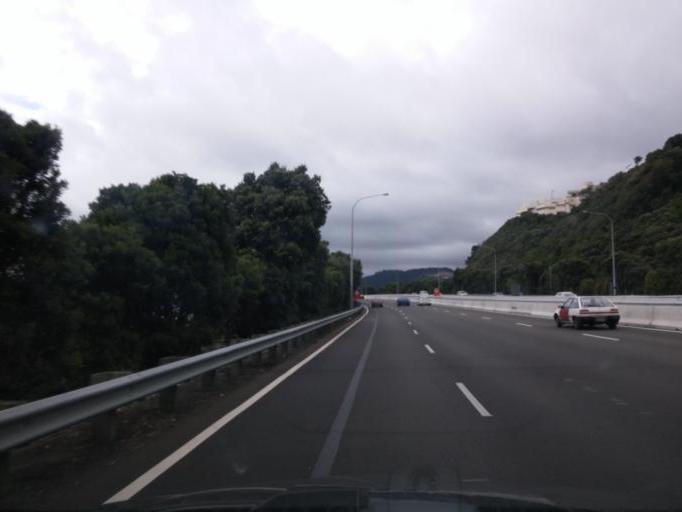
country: NZ
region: Wellington
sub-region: Wellington City
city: Wellington
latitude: -41.2498
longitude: 174.8084
